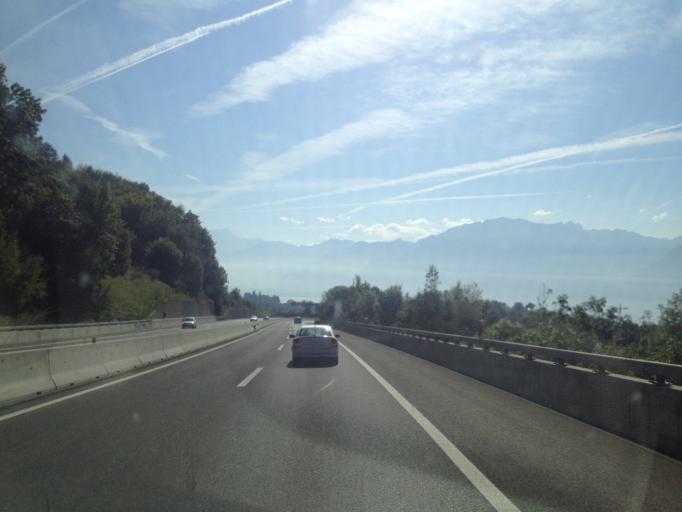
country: CH
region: Vaud
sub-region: Riviera-Pays-d'Enhaut District
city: Blonay
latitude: 46.4840
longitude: 6.8858
